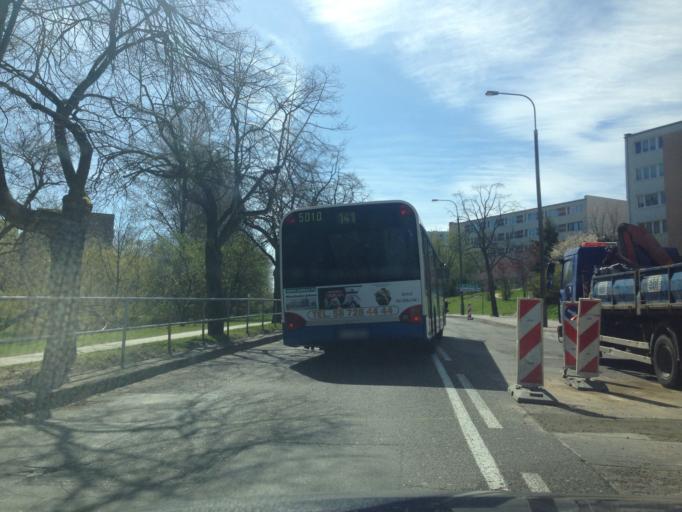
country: PL
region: Pomeranian Voivodeship
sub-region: Gdynia
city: Gdynia
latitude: 54.5002
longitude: 18.5126
